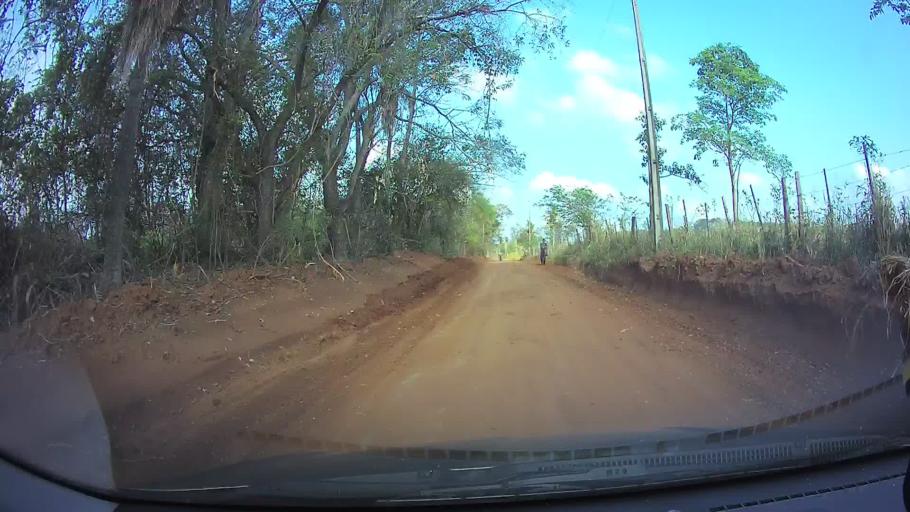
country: PY
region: Cordillera
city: Arroyos y Esteros
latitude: -25.0198
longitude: -57.1937
